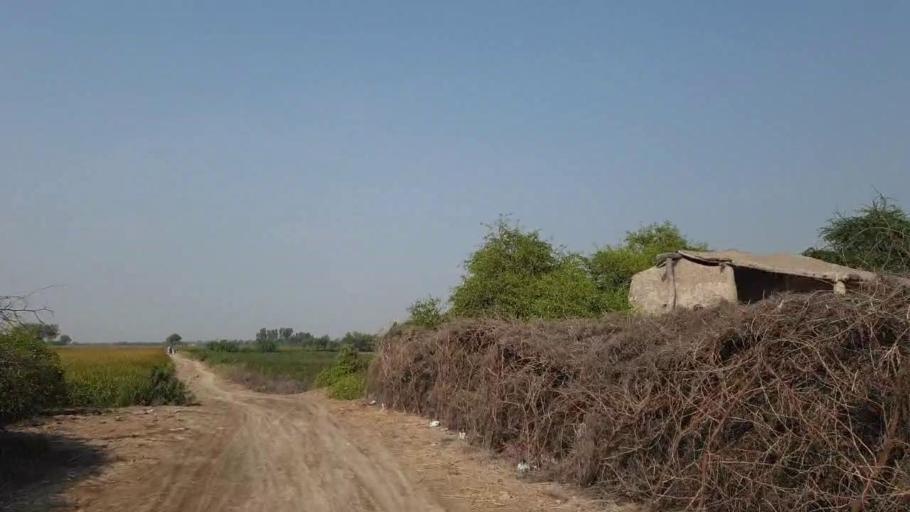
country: PK
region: Sindh
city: Matli
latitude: 24.9587
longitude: 68.5592
